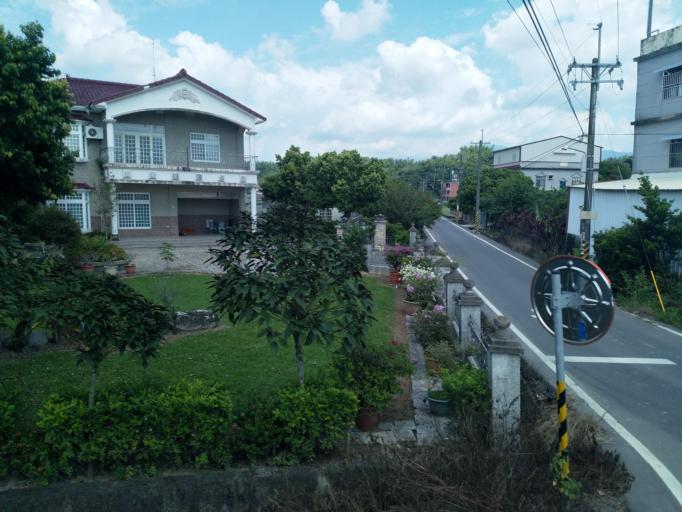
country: TW
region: Taiwan
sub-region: Pingtung
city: Pingtung
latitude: 22.8857
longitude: 120.5538
